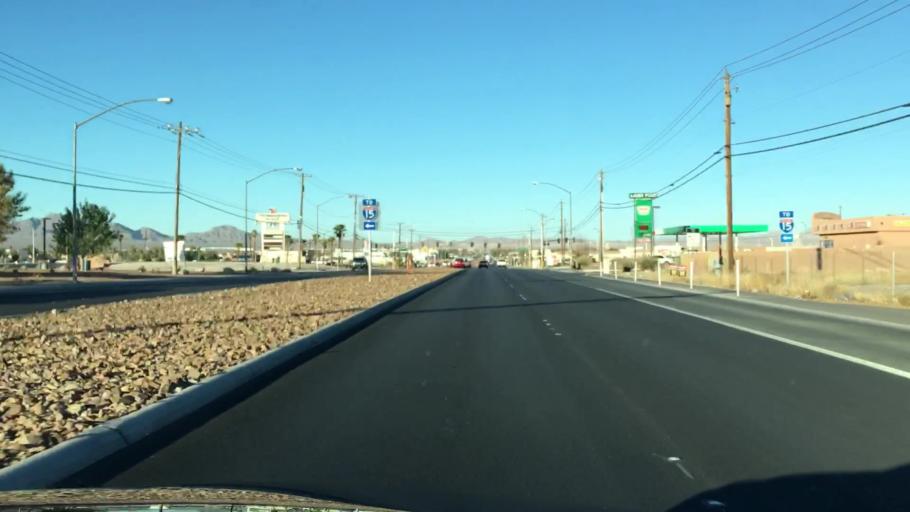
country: US
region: Nevada
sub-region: Clark County
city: Sunrise Manor
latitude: 36.2243
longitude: -115.0821
